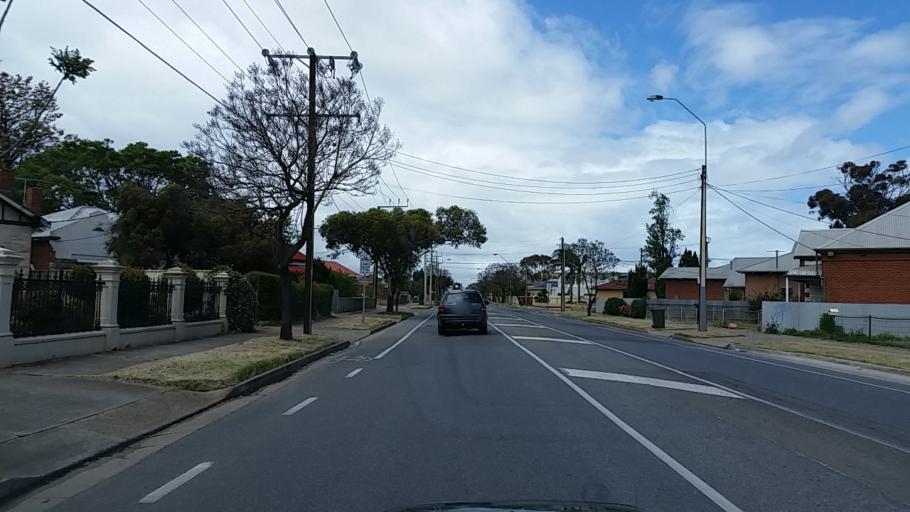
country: AU
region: South Australia
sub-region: Charles Sturt
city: Woodville
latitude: -34.8782
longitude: 138.5505
